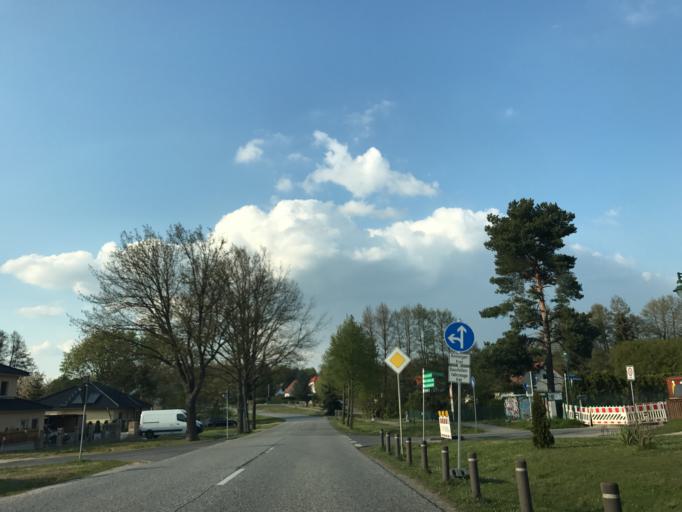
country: DE
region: Brandenburg
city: Wustermark
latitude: 52.5216
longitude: 12.9814
